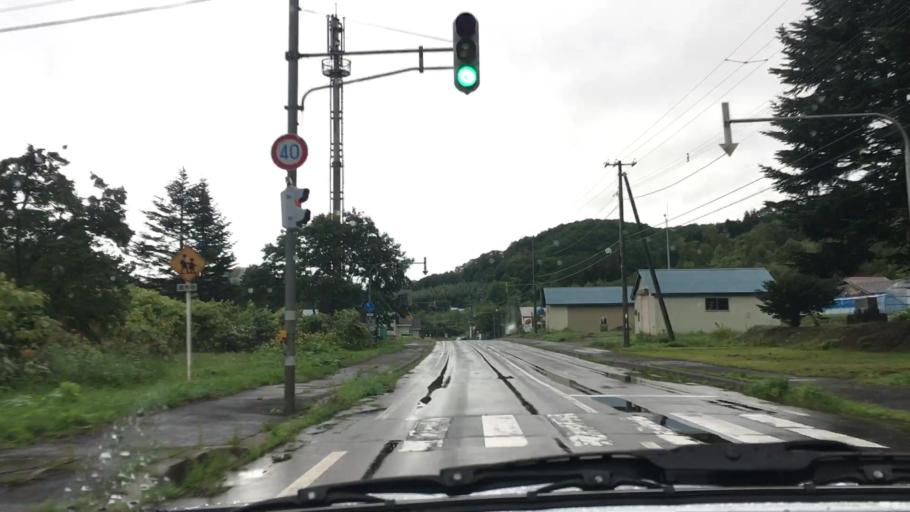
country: JP
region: Hokkaido
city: Niseko Town
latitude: 42.6474
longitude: 140.7340
